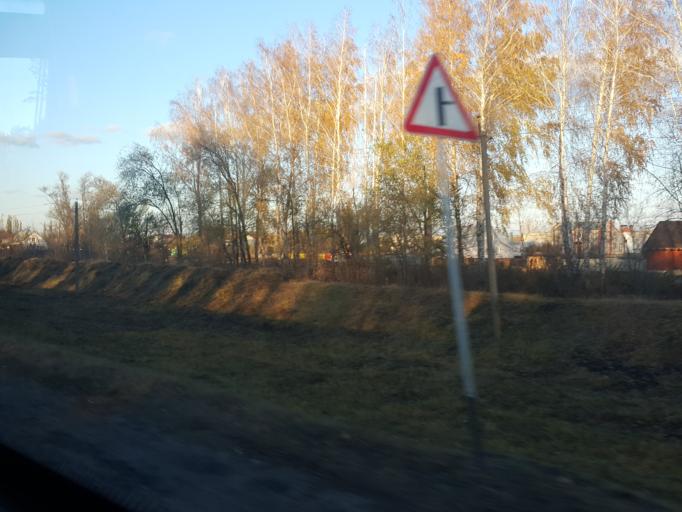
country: RU
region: Tambov
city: Bokino
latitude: 52.6218
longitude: 41.4439
